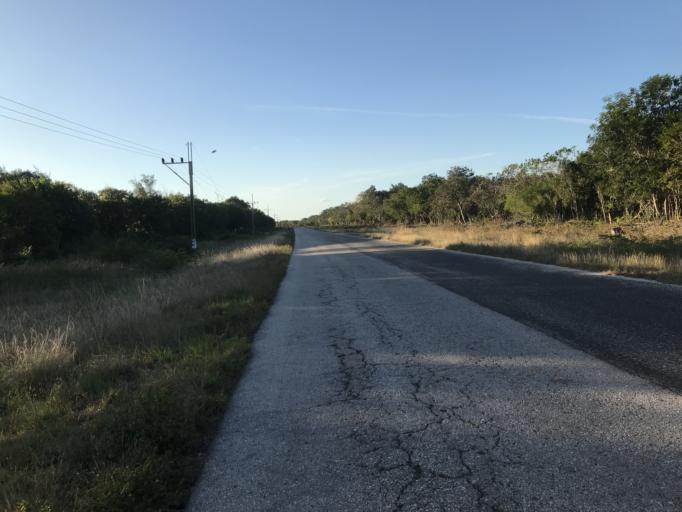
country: CU
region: Cienfuegos
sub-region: Municipio de Aguada de Pasajeros
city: Aguada de Pasajeros
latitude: 22.0733
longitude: -81.0572
